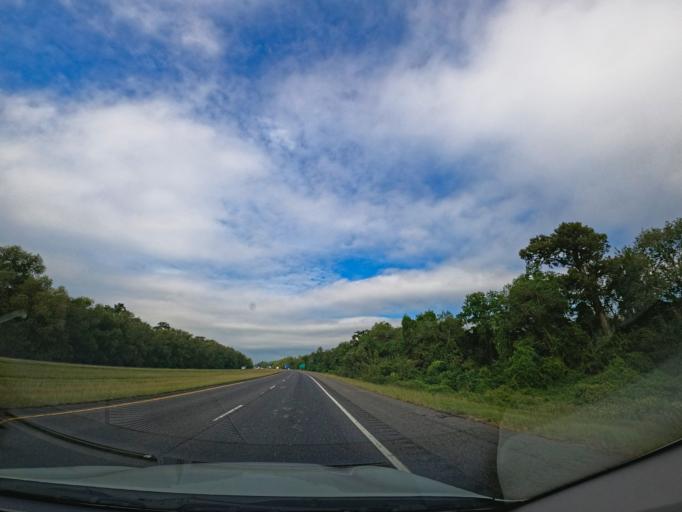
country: US
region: Louisiana
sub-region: Saint Mary Parish
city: Morgan City
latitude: 29.6970
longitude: -91.1602
